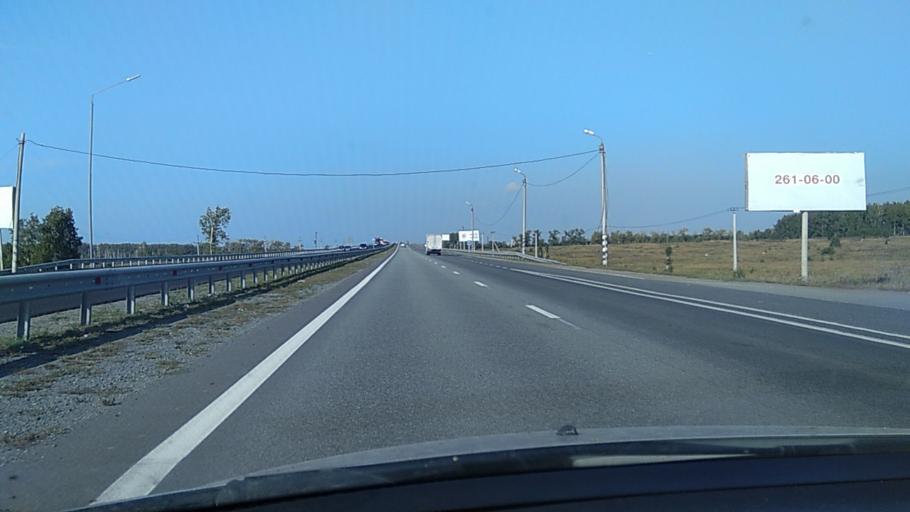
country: RU
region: Chelyabinsk
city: Sargazy
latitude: 55.0447
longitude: 61.3038
